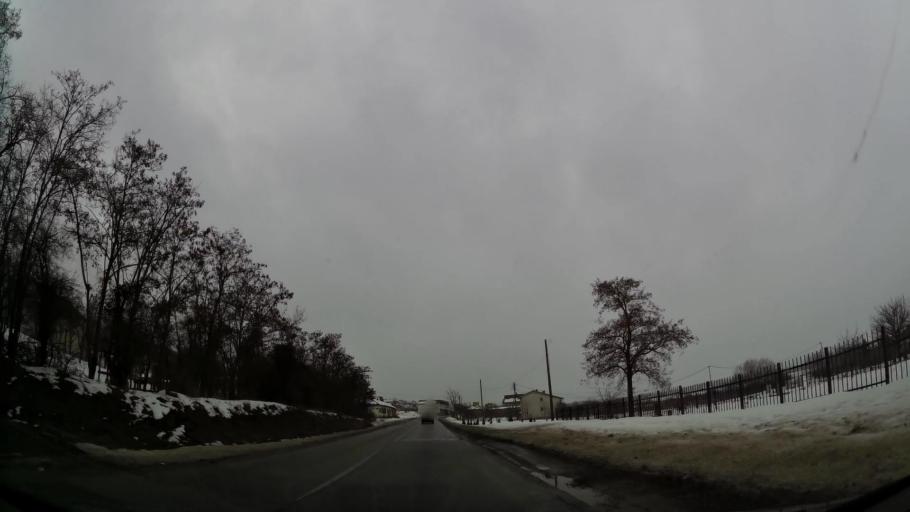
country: XK
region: Pristina
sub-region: Komuna e Prishtines
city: Pristina
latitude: 42.7307
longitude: 21.1428
